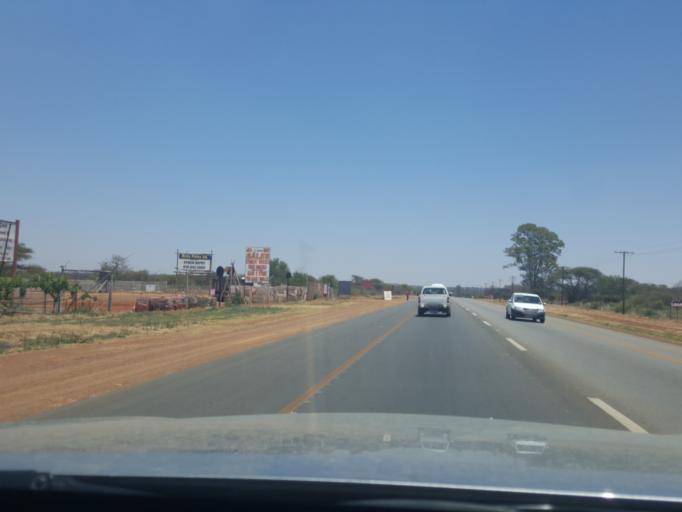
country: ZA
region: North-West
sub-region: Ngaka Modiri Molema District Municipality
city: Zeerust
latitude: -25.5553
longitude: 26.0687
